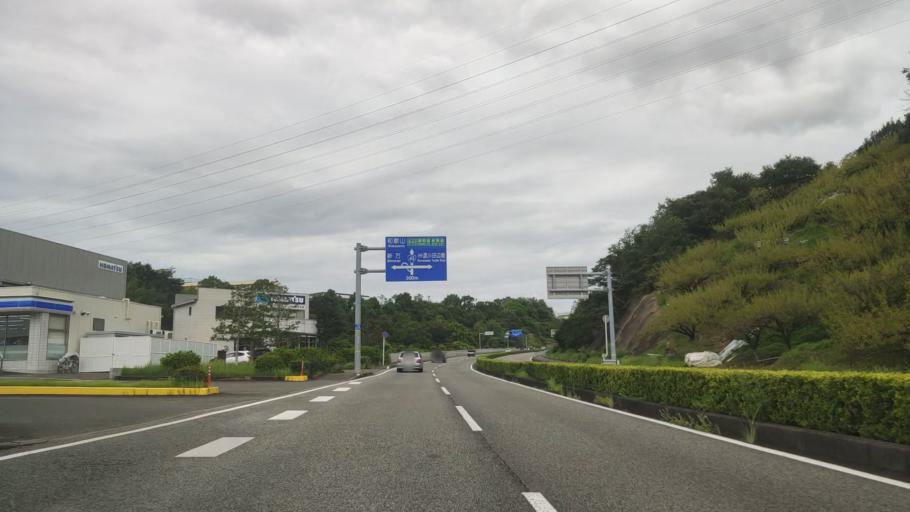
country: JP
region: Wakayama
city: Tanabe
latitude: 33.7285
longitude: 135.4010
